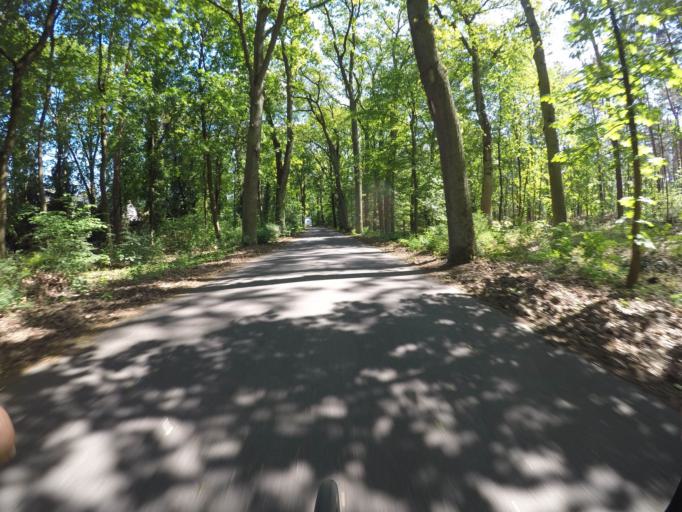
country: DE
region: Berlin
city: Wannsee
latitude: 52.4206
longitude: 13.1515
